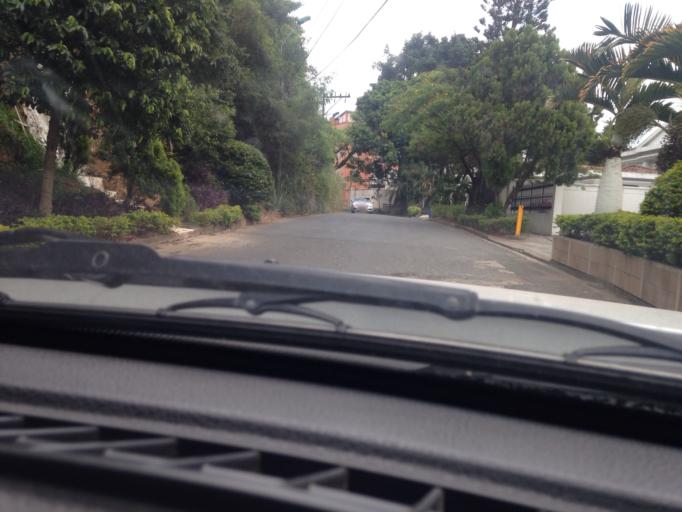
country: CO
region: Valle del Cauca
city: Cali
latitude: 3.4886
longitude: -76.5269
